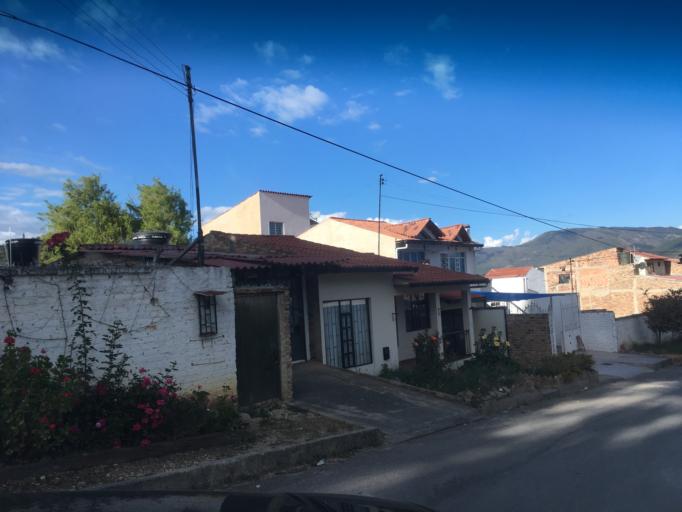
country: CO
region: Boyaca
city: Tibasosa
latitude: 5.7441
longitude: -73.0054
